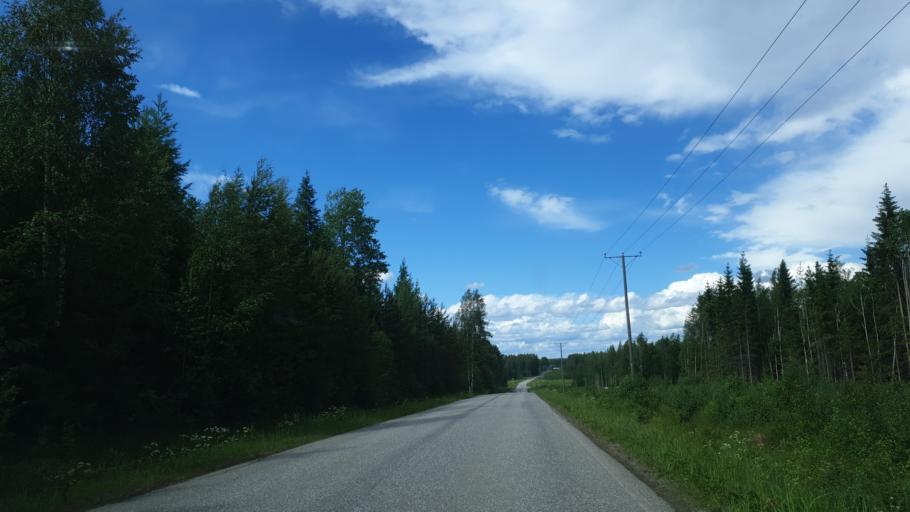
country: FI
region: Northern Savo
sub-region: Koillis-Savo
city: Kaavi
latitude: 62.9815
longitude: 28.7429
